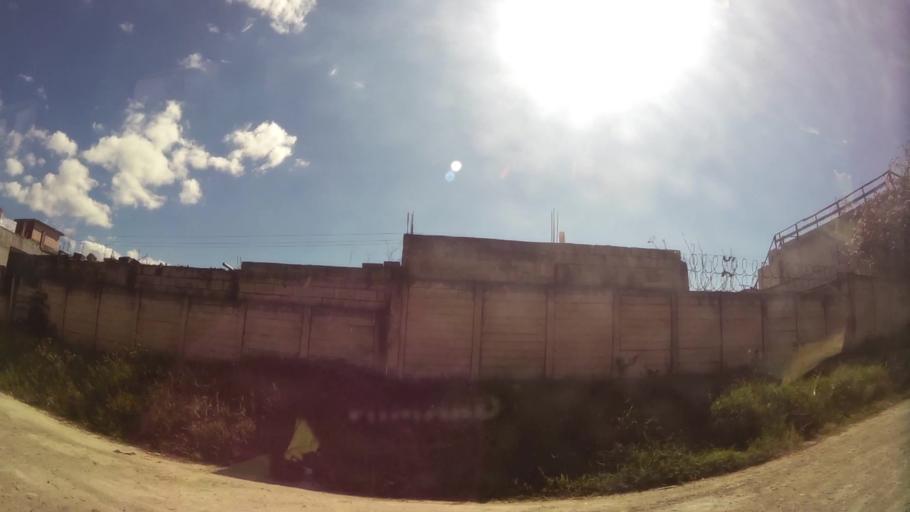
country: GT
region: Guatemala
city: Petapa
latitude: 14.4972
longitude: -90.5637
